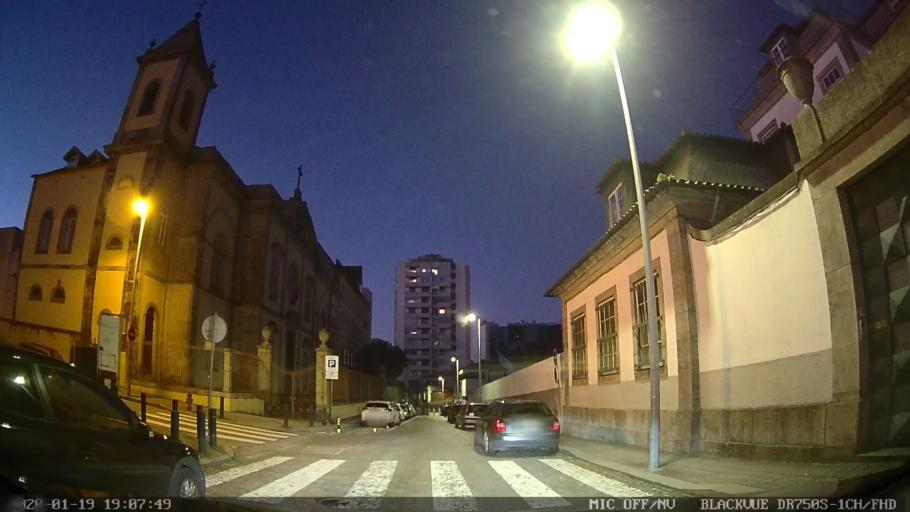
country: PT
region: Porto
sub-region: Porto
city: Porto
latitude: 41.1498
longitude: -8.6277
